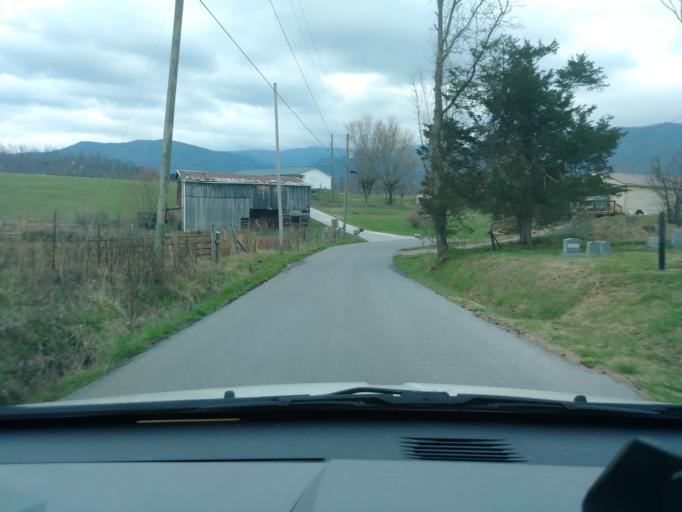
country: US
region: Tennessee
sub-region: Greene County
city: Tusculum
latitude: 36.0878
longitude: -82.7463
